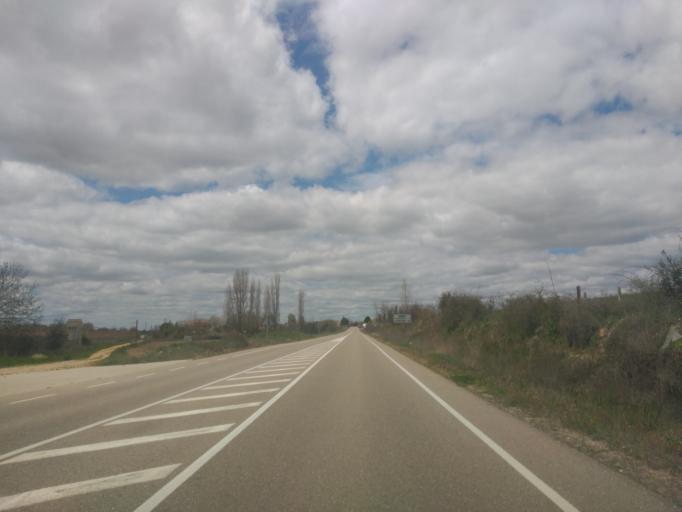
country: ES
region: Castille and Leon
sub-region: Provincia de Salamanca
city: Valverdon
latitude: 41.0435
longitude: -5.7606
